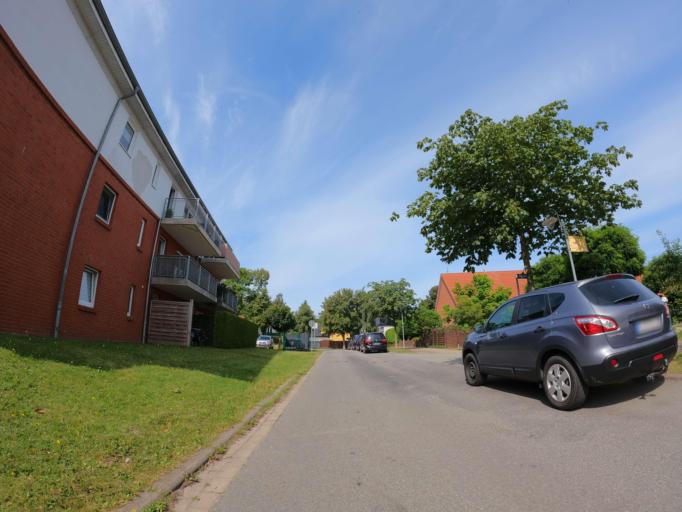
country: DE
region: Mecklenburg-Vorpommern
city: Kramerhof
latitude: 54.3510
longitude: 13.0709
